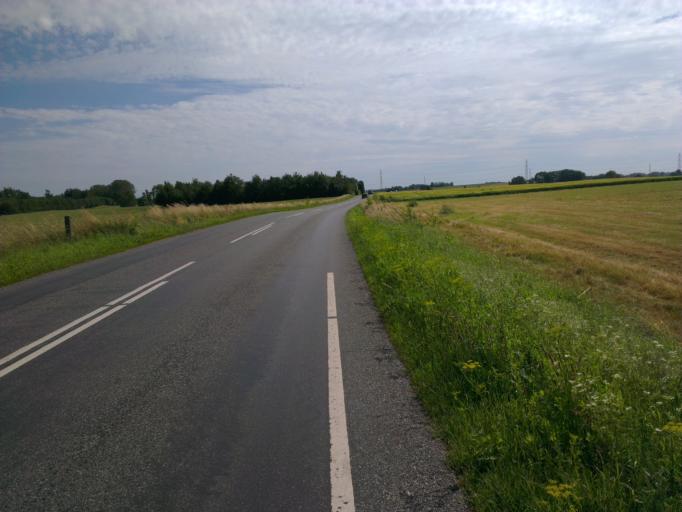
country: DK
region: Capital Region
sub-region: Frederikssund Kommune
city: Frederikssund
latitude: 55.8086
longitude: 12.0230
